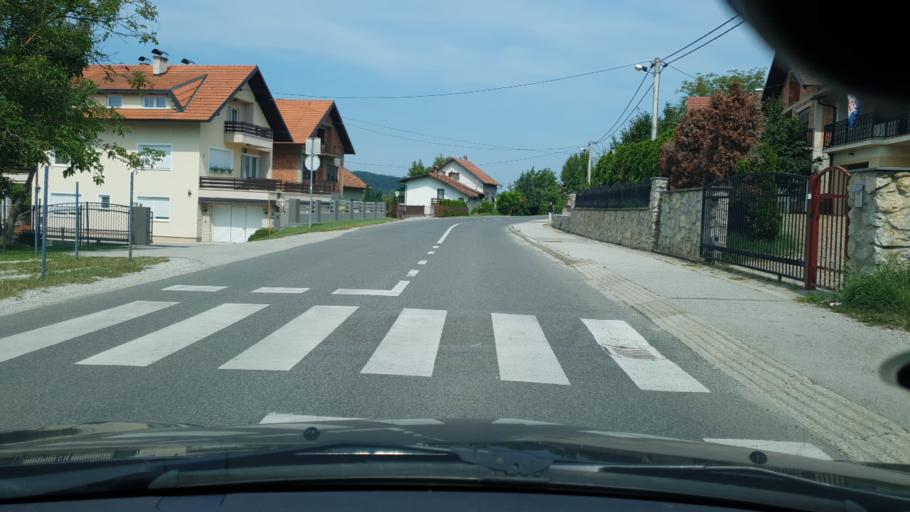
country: HR
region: Krapinsko-Zagorska
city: Marija Bistrica
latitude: 46.0076
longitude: 16.1118
